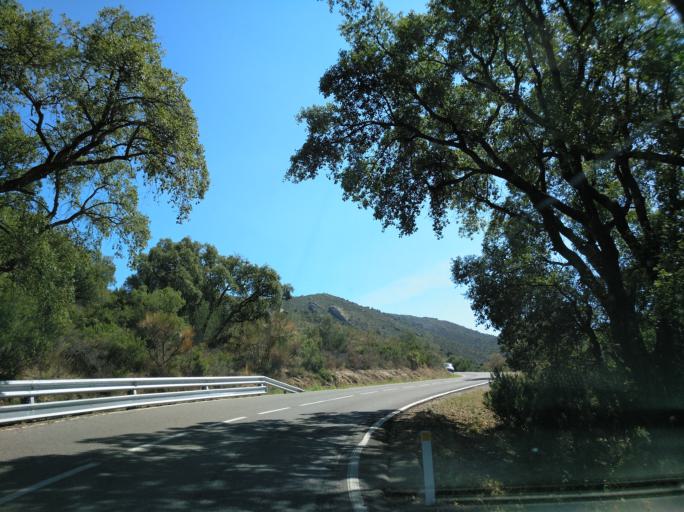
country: ES
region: Catalonia
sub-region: Provincia de Girona
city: Pau
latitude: 42.3306
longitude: 3.1150
